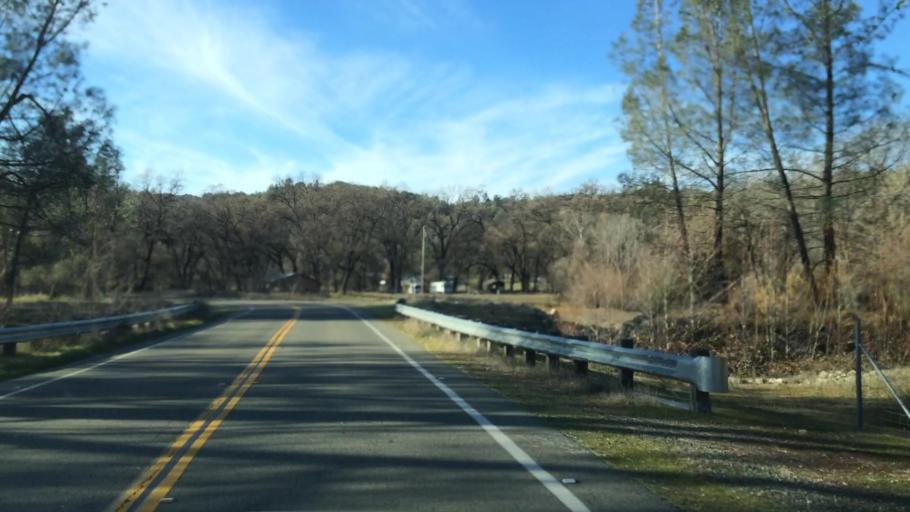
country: US
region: California
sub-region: Nevada County
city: Penn Valley
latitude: 39.2118
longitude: -121.1625
